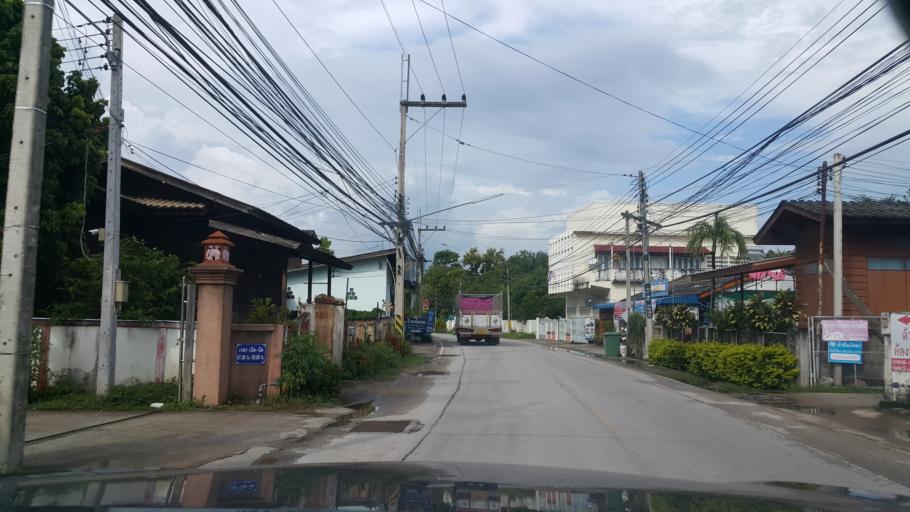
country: TH
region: Lampang
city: Thoen
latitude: 17.6122
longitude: 99.2177
